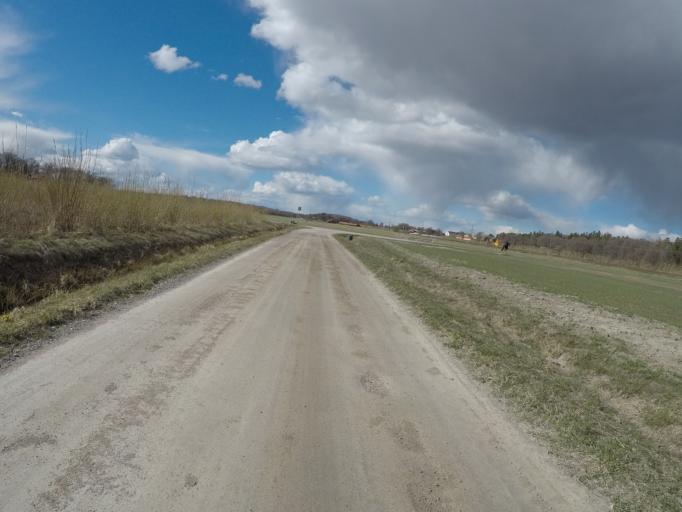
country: SE
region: Vaestmanland
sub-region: Hallstahammars Kommun
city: Kolback
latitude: 59.5116
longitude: 16.2548
